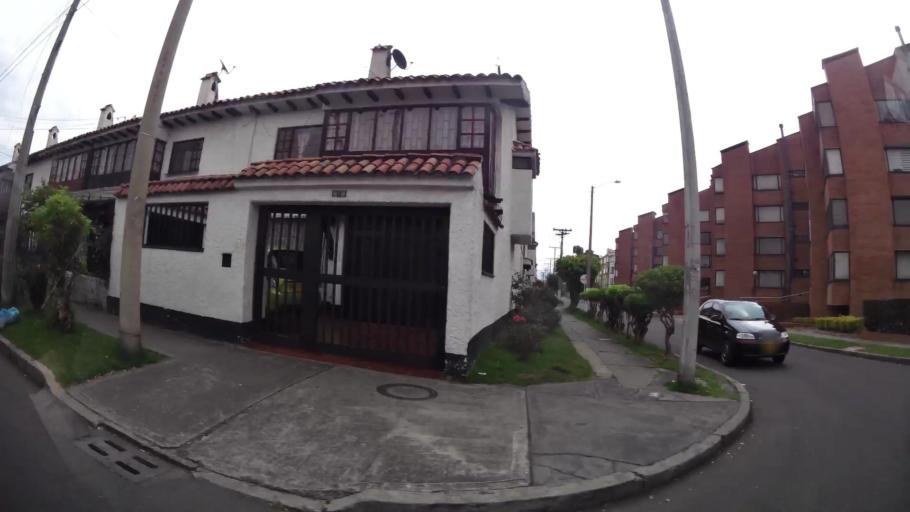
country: CO
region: Bogota D.C.
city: Barrio San Luis
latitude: 4.6897
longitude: -74.0741
